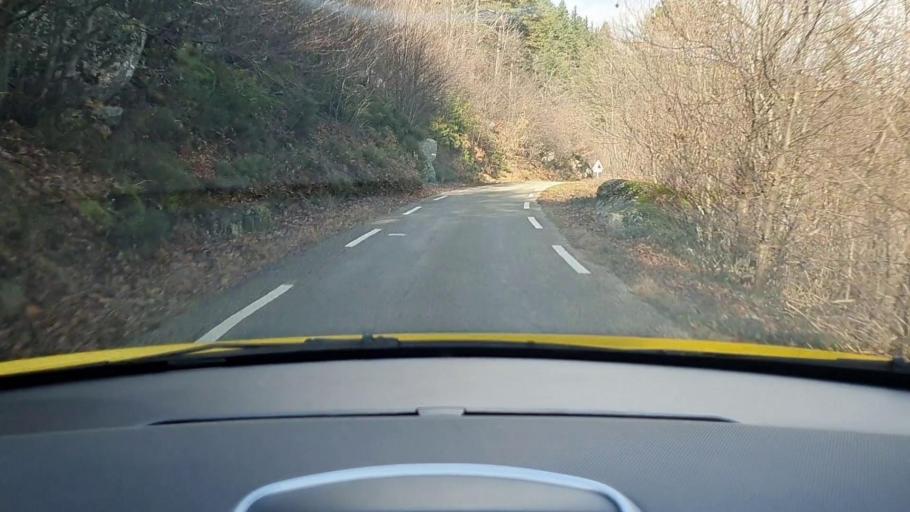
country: FR
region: Languedoc-Roussillon
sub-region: Departement du Gard
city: Branoux-les-Taillades
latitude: 44.3569
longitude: 3.9267
